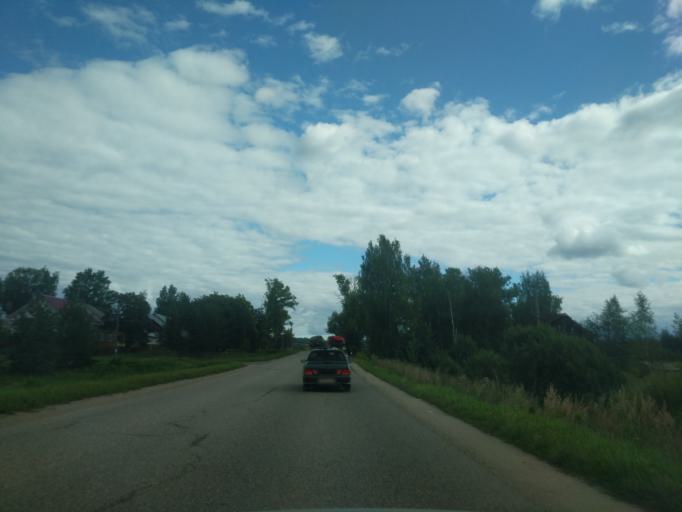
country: RU
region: Kostroma
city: Sudislavl'
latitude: 57.8791
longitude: 41.7233
